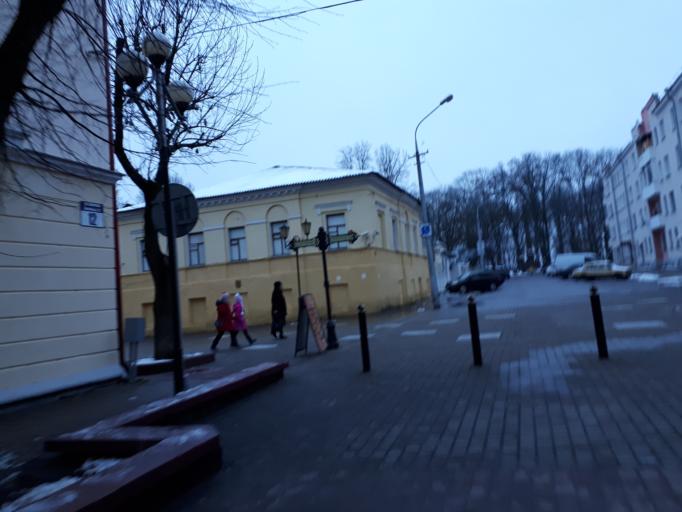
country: BY
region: Vitebsk
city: Vitebsk
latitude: 55.1994
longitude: 30.2054
